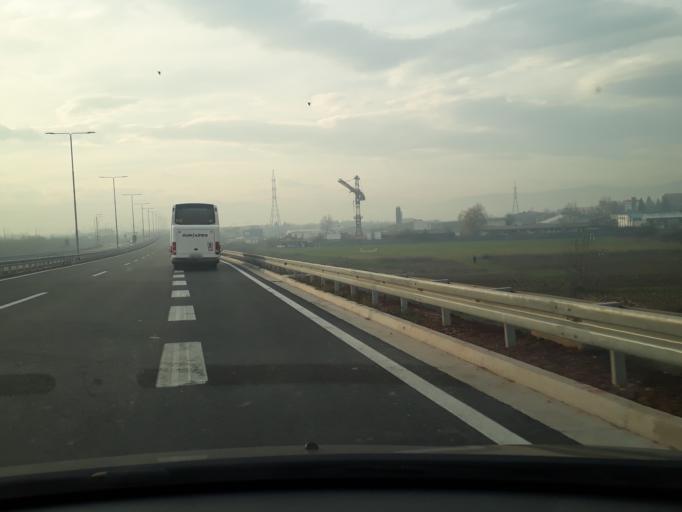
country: BA
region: Federation of Bosnia and Herzegovina
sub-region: Kanton Sarajevo
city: Sarajevo
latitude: 43.8516
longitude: 18.3331
